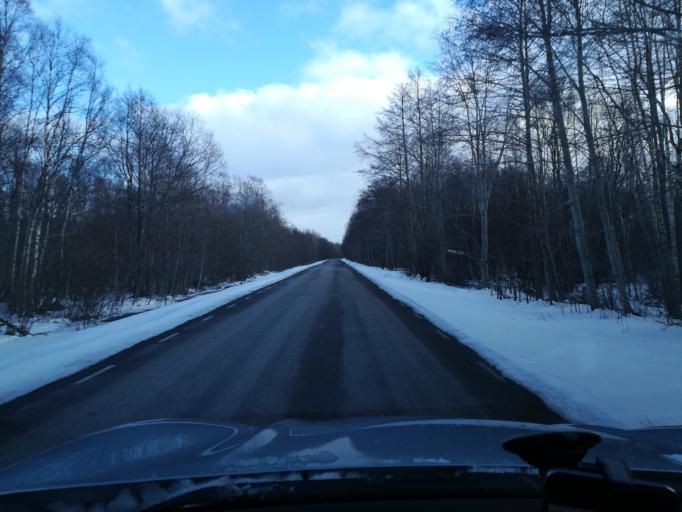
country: EE
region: Harju
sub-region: Keila linn
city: Keila
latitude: 59.4431
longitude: 24.3863
